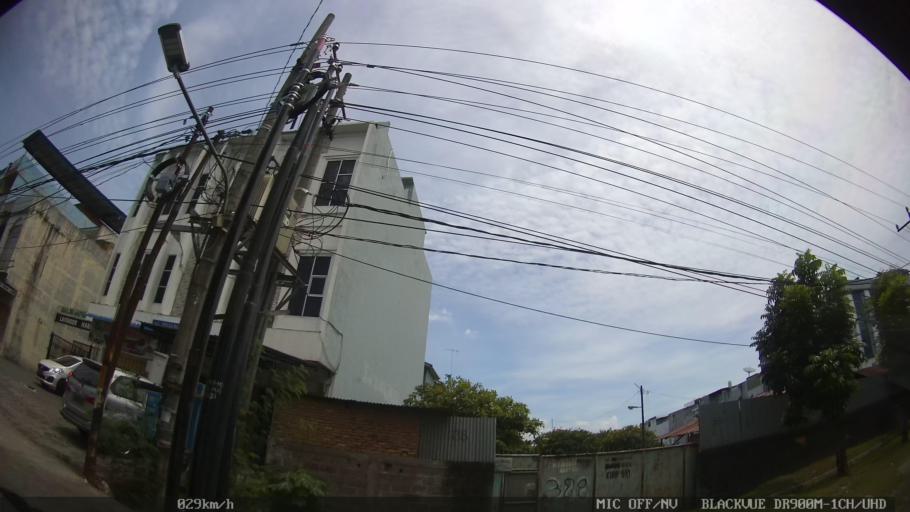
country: ID
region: North Sumatra
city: Sunggal
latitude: 3.5755
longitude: 98.6155
